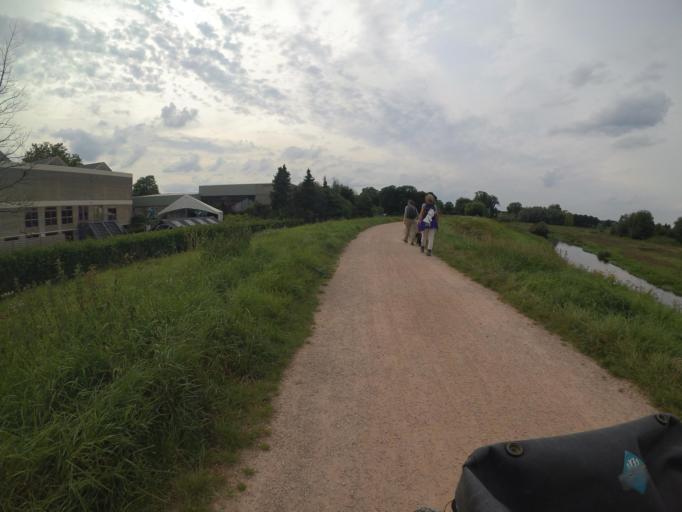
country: NL
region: Limburg
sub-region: Gemeente Gennep
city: Gennep
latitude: 51.6997
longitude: 5.9773
